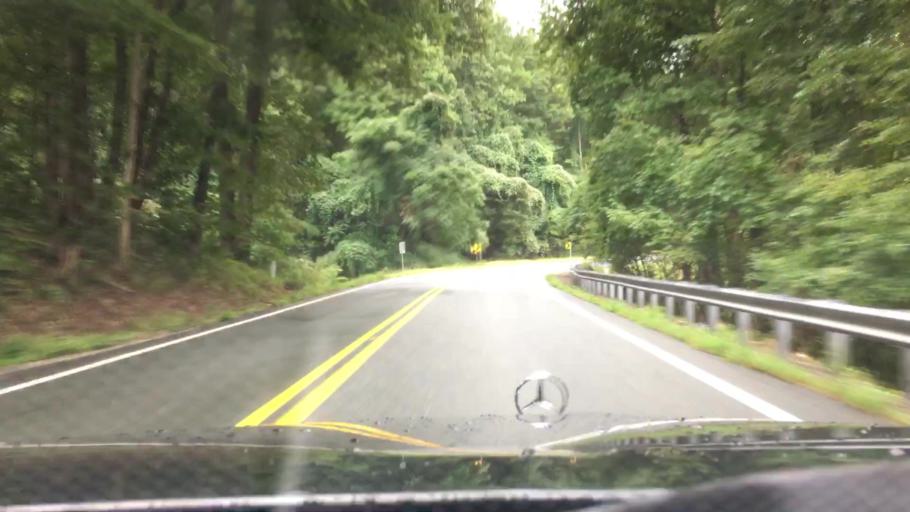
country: US
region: Virginia
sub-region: Nelson County
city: Nellysford
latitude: 37.8613
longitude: -78.9204
